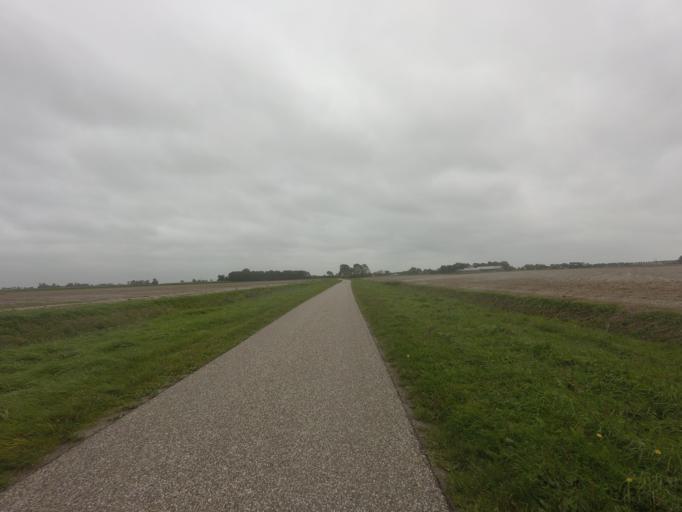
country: NL
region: Friesland
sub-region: Gemeente Ferwerderadiel
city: Ferwert
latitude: 53.3422
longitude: 5.8576
